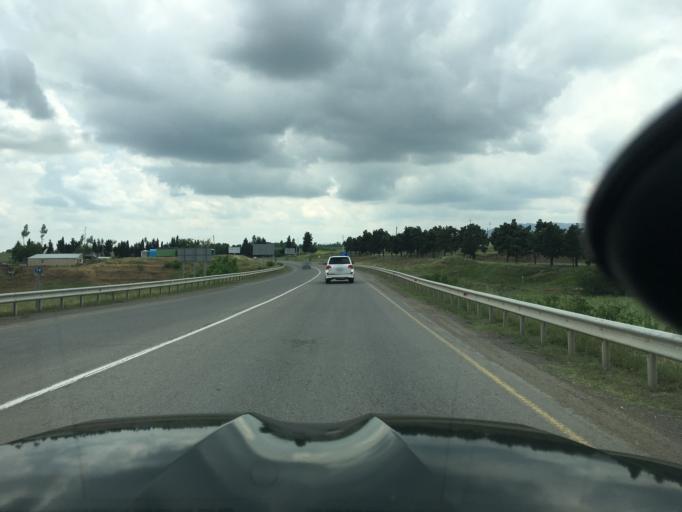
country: AZ
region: Tovuz
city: Tovuz
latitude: 40.9780
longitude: 45.6691
